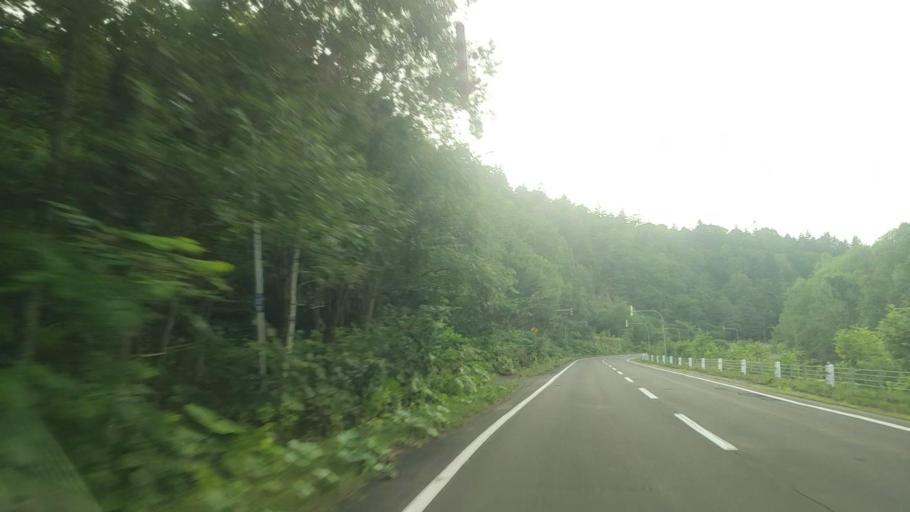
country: JP
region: Hokkaido
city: Bibai
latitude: 43.1294
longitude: 142.0962
